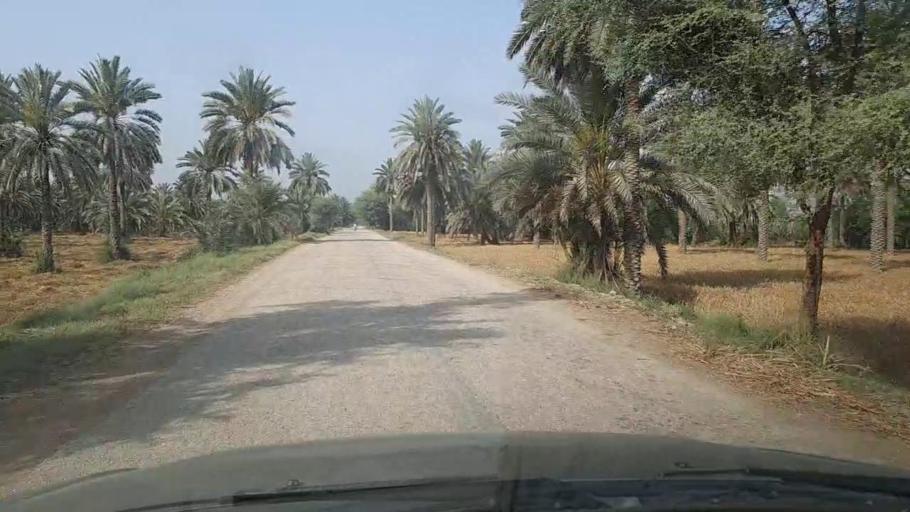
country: PK
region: Sindh
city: Pir jo Goth
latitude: 27.5400
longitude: 68.5190
